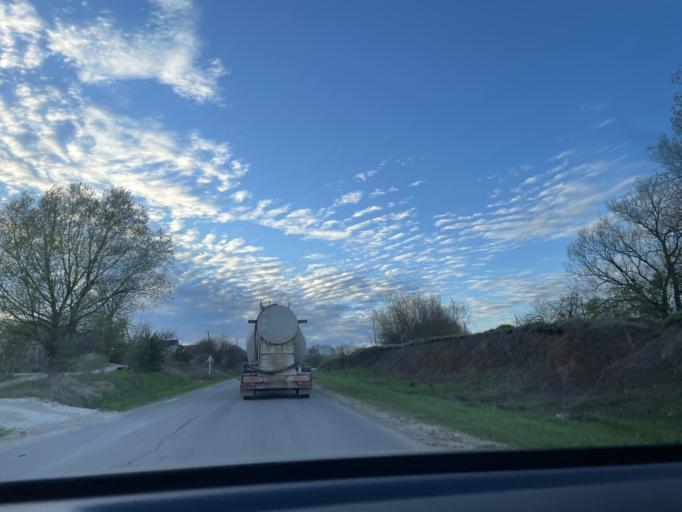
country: RU
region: Moskovskaya
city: Serpukhov
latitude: 54.8259
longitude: 37.4292
